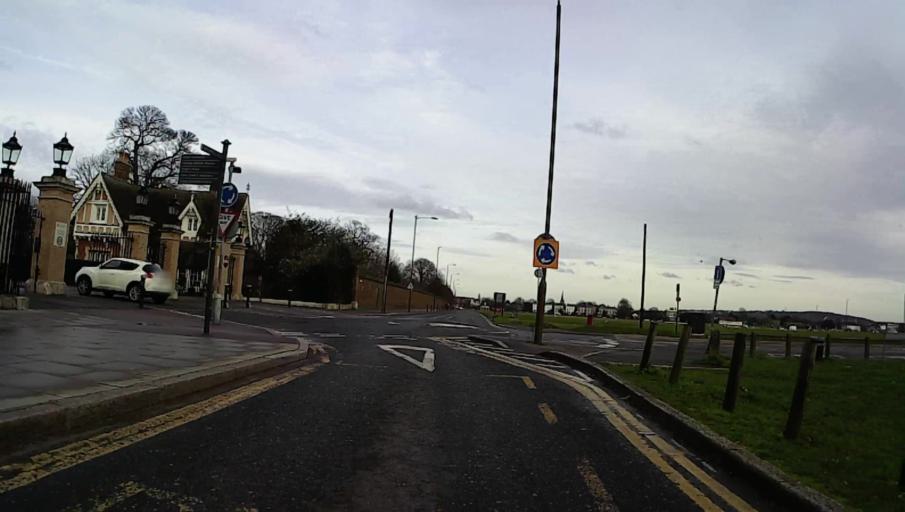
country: GB
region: England
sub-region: Greater London
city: Blackheath
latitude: 51.4729
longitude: 0.0031
